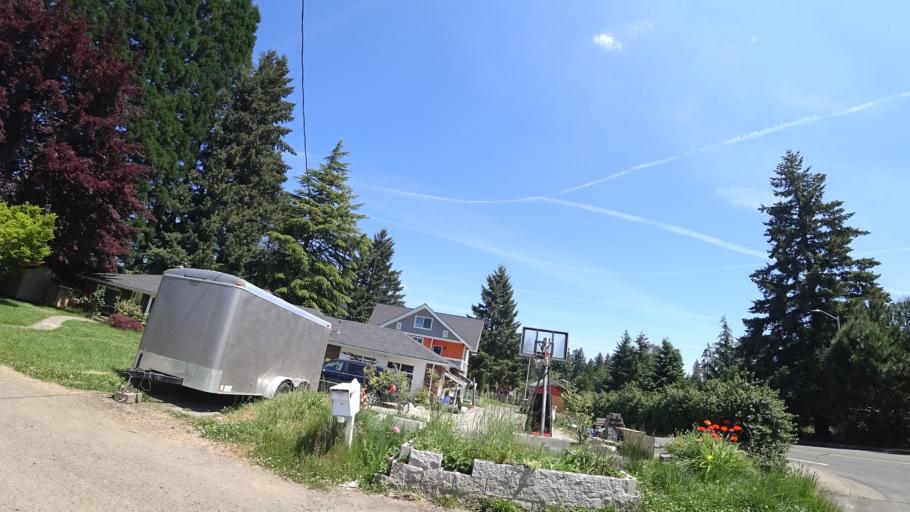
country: US
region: Oregon
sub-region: Washington County
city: King City
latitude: 45.4279
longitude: -122.8099
